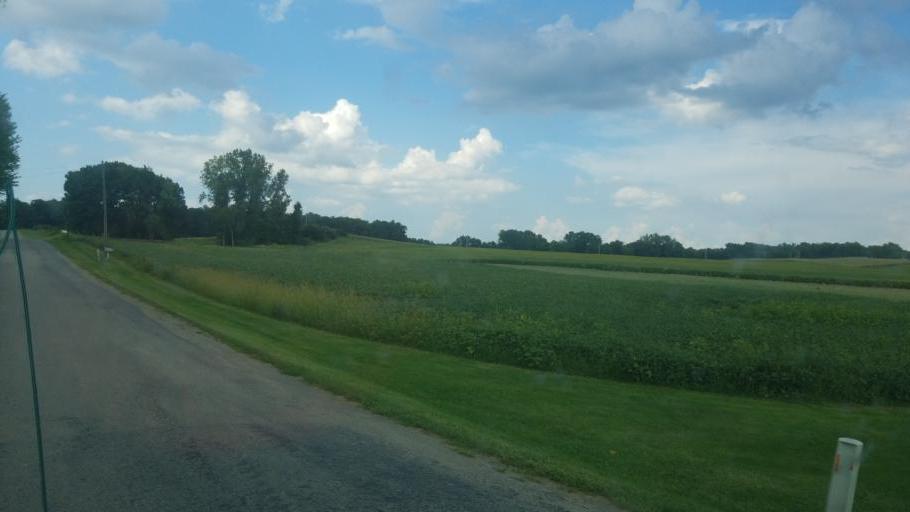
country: US
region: Ohio
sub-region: Huron County
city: Plymouth
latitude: 40.9956
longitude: -82.7082
